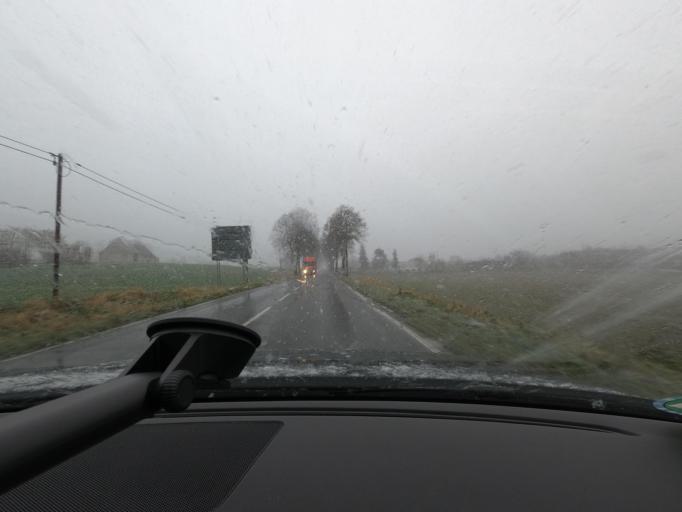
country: DE
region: North Rhine-Westphalia
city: Marsberg
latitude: 51.4978
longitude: 8.9175
